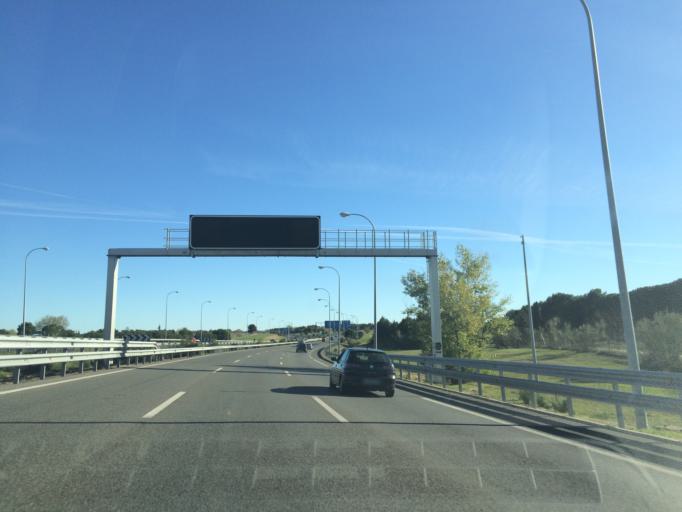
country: ES
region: Madrid
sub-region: Provincia de Madrid
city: Alcorcon
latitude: 40.3804
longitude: -3.8105
